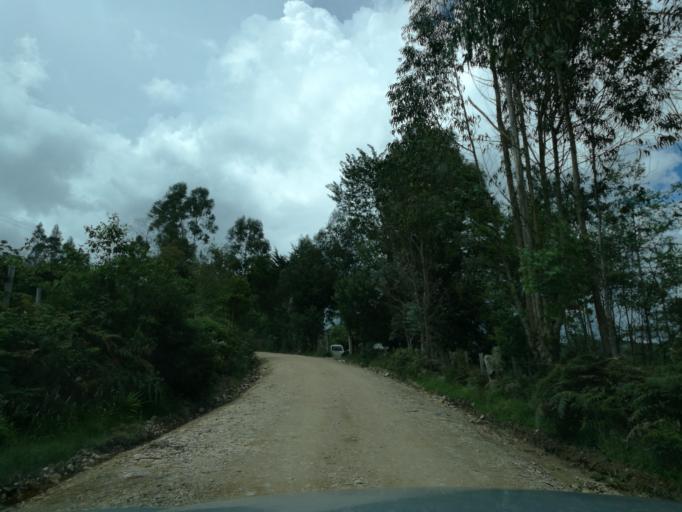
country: CO
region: Boyaca
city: Arcabuco
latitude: 5.7541
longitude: -73.4480
